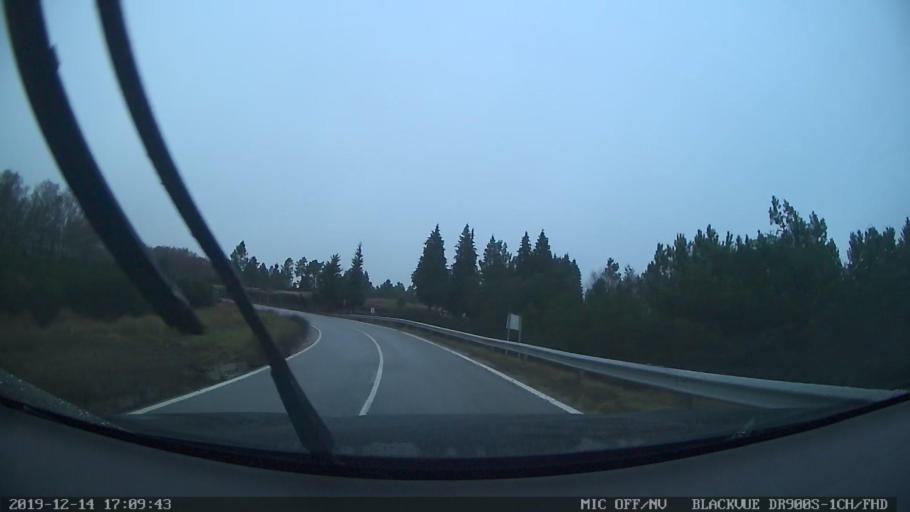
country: PT
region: Vila Real
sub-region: Vila Pouca de Aguiar
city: Vila Pouca de Aguiar
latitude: 41.4785
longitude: -7.6038
